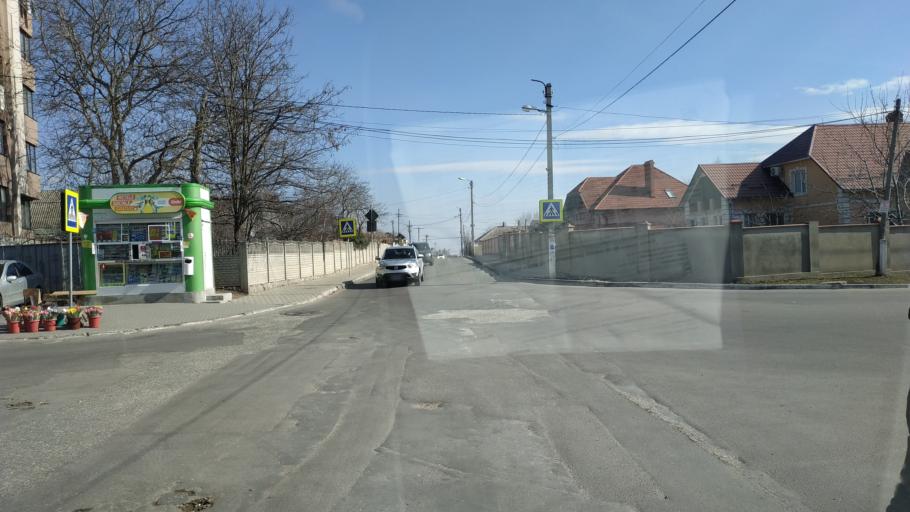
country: MD
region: Chisinau
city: Vatra
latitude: 47.0161
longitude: 28.7476
